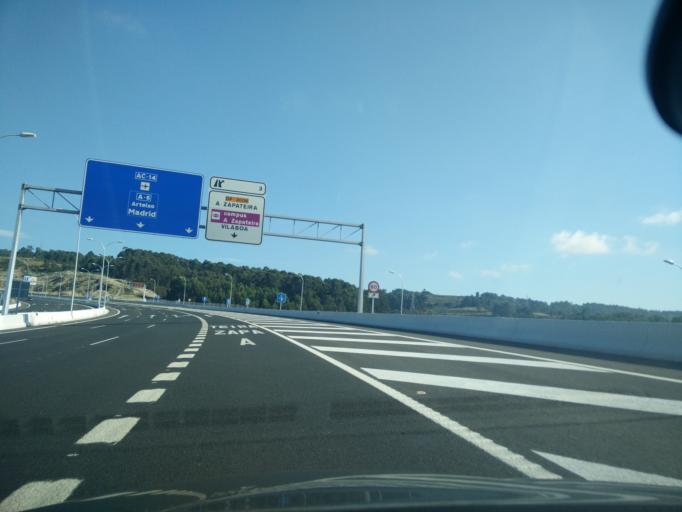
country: ES
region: Galicia
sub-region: Provincia da Coruna
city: A Coruna
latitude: 43.3270
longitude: -8.4228
